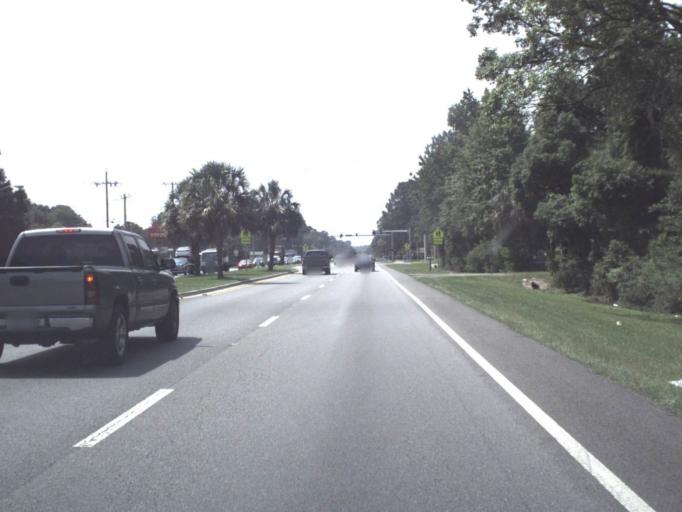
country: US
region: Florida
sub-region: Duval County
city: Jacksonville
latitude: 30.3885
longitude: -81.7343
